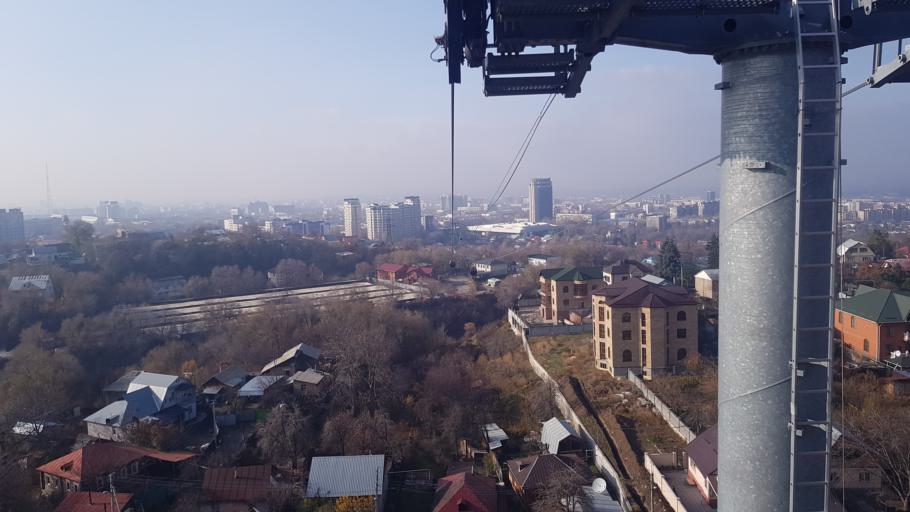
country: KZ
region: Almaty Qalasy
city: Almaty
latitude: 43.2369
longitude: 76.9703
